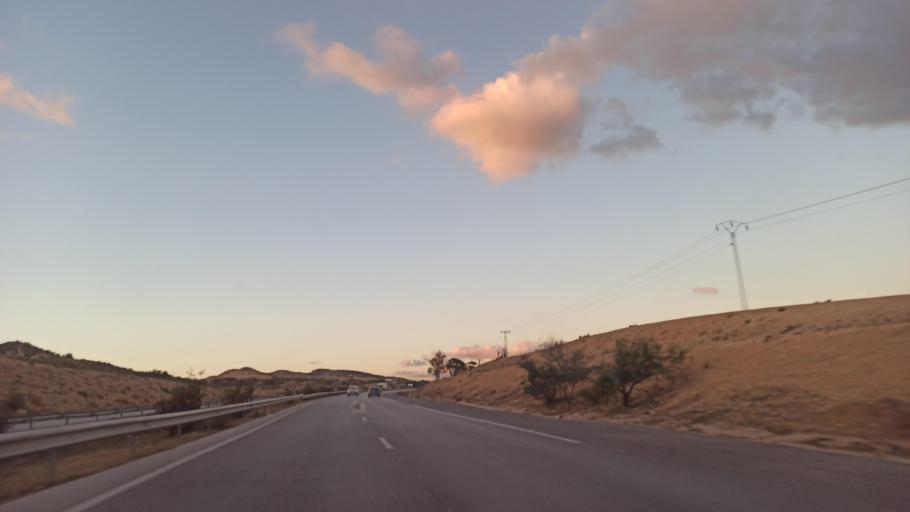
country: TN
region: Susah
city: Harqalah
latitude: 36.2270
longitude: 10.4148
